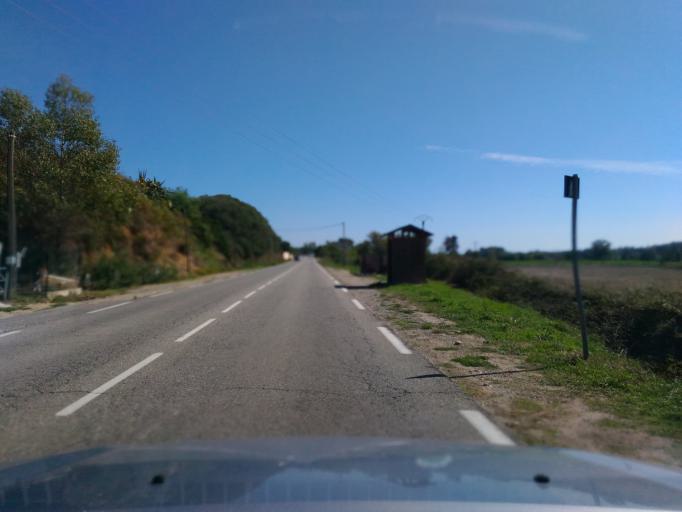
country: FR
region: Corsica
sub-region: Departement de la Haute-Corse
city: Aleria
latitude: 42.1135
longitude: 9.5043
